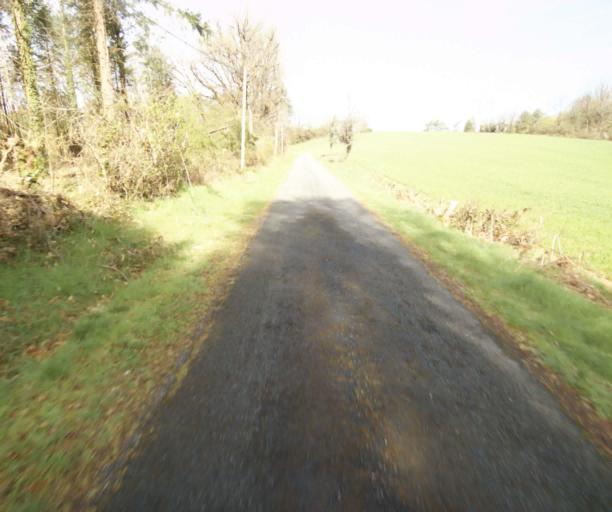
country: FR
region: Limousin
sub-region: Departement de la Correze
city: Laguenne
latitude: 45.2841
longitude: 1.8282
